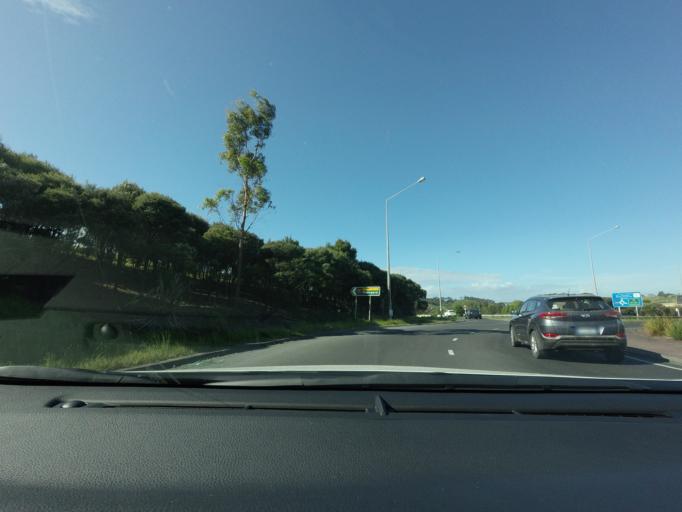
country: NZ
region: Auckland
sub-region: Auckland
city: Rothesay Bay
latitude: -36.6255
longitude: 174.6615
